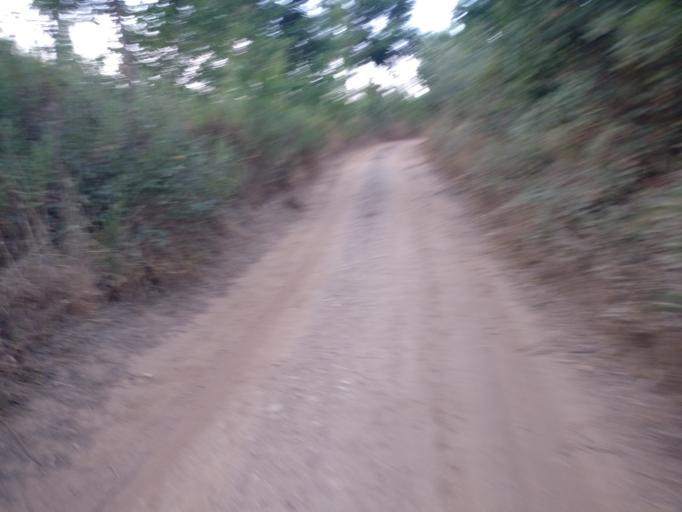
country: PT
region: Beja
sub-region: Odemira
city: Odemira
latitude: 37.7118
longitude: -8.5173
